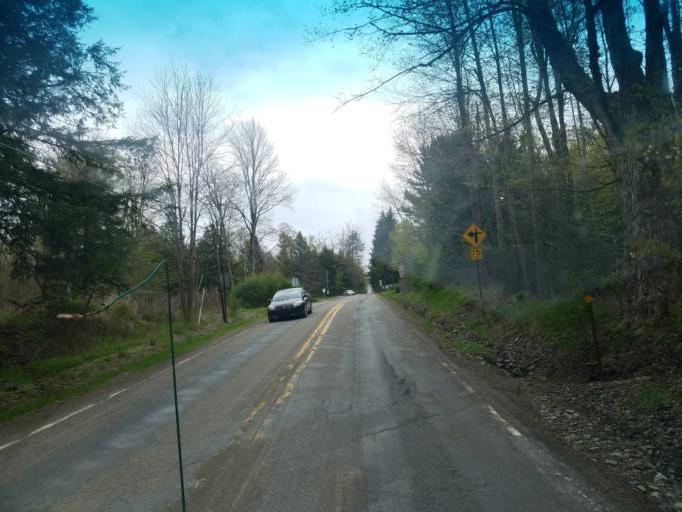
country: US
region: Pennsylvania
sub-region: Tioga County
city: Wellsboro
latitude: 41.6951
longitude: -77.4338
